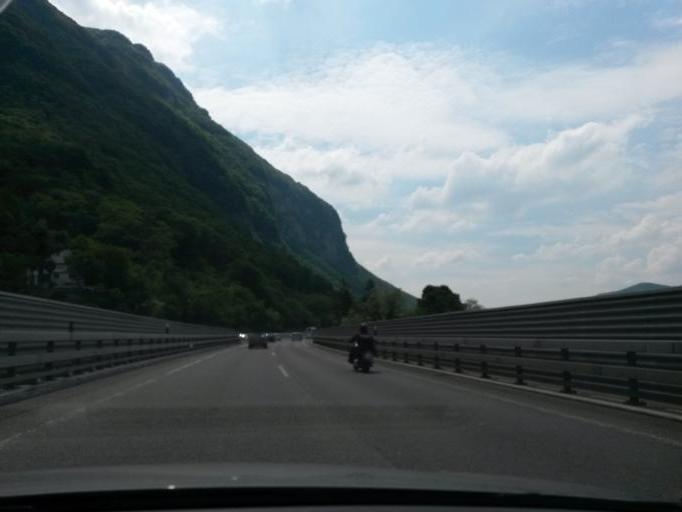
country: CH
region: Ticino
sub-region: Lugano District
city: Melano
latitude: 45.9171
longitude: 8.9849
